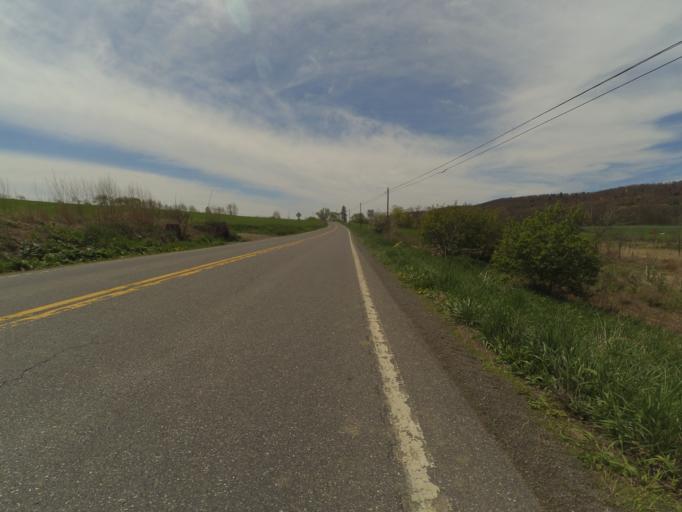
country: US
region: Pennsylvania
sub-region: Centre County
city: Stormstown
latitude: 40.7358
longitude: -78.0933
